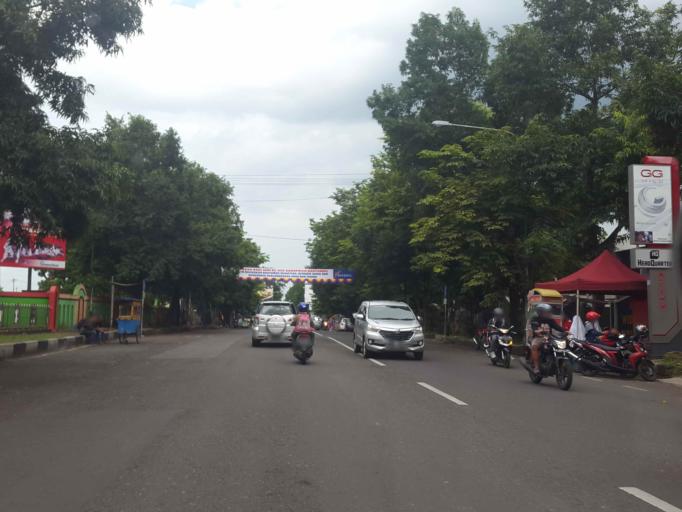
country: ID
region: Central Java
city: Purwokerto
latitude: -7.4173
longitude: 109.2498
